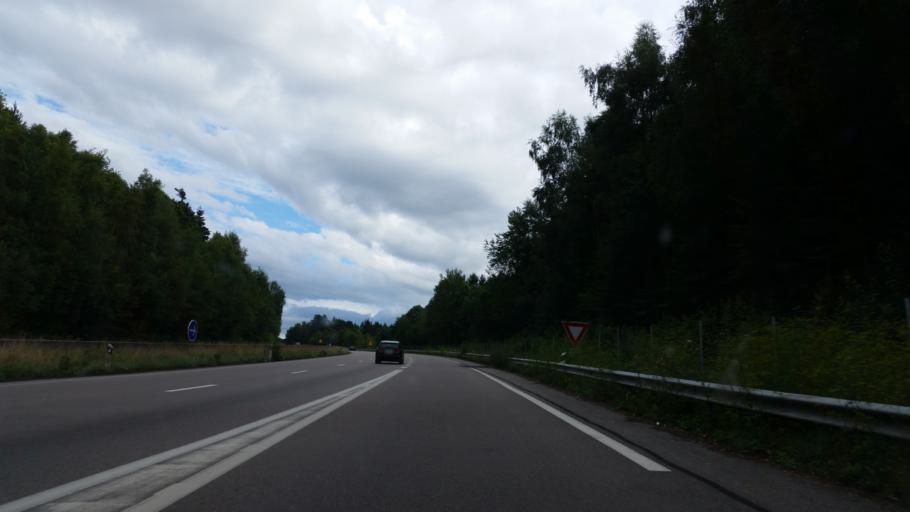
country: FR
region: Lorraine
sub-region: Departement des Vosges
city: Epinal
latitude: 48.1732
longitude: 6.4826
